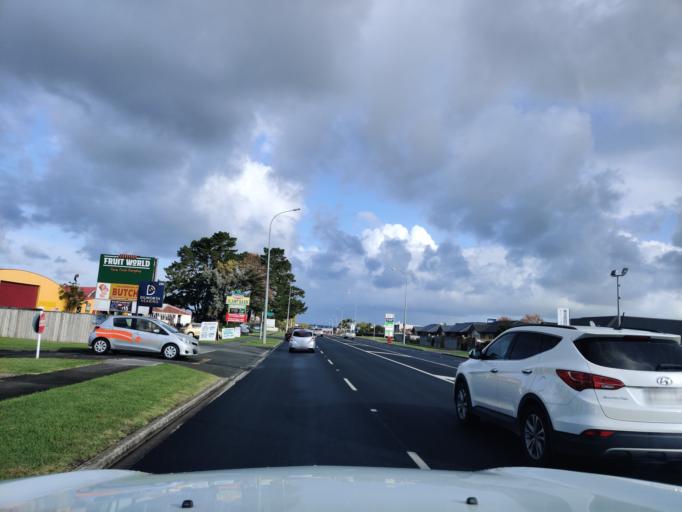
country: NZ
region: Auckland
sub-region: Auckland
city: Pakuranga
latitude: -36.9225
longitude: 174.9131
